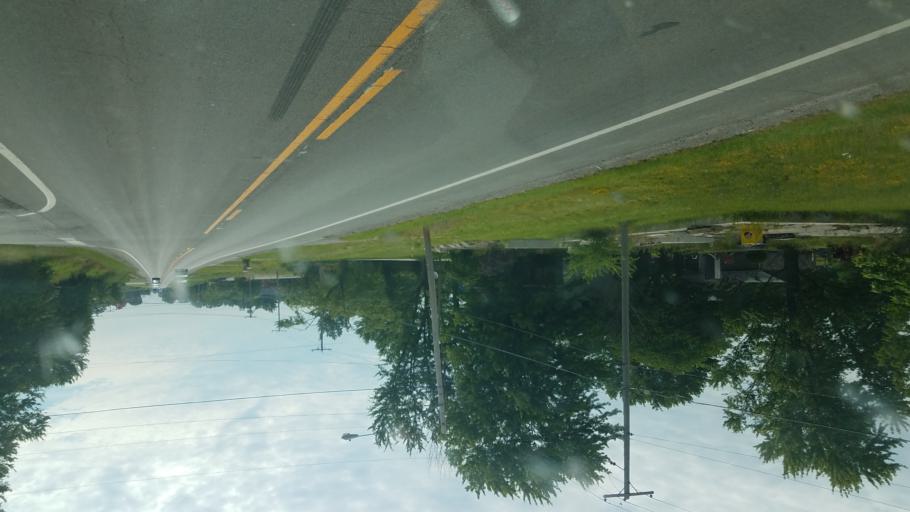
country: US
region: Ohio
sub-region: Lorain County
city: Eaton Estates
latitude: 41.3137
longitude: -81.9915
